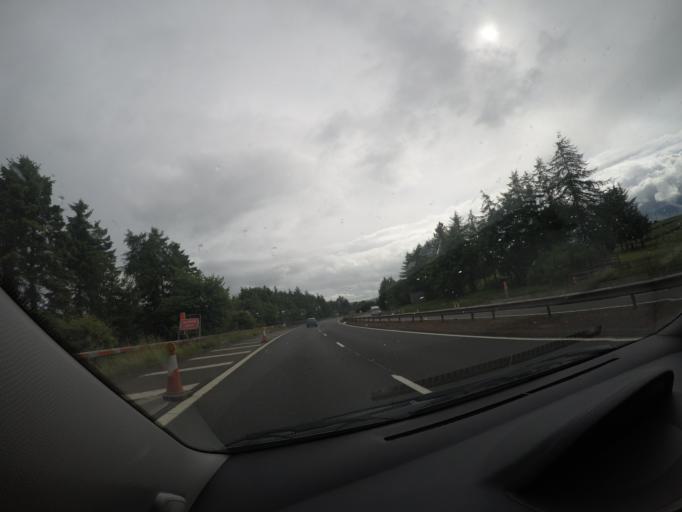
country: GB
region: Scotland
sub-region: Falkirk
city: Denny
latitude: 56.0035
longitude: -3.9161
